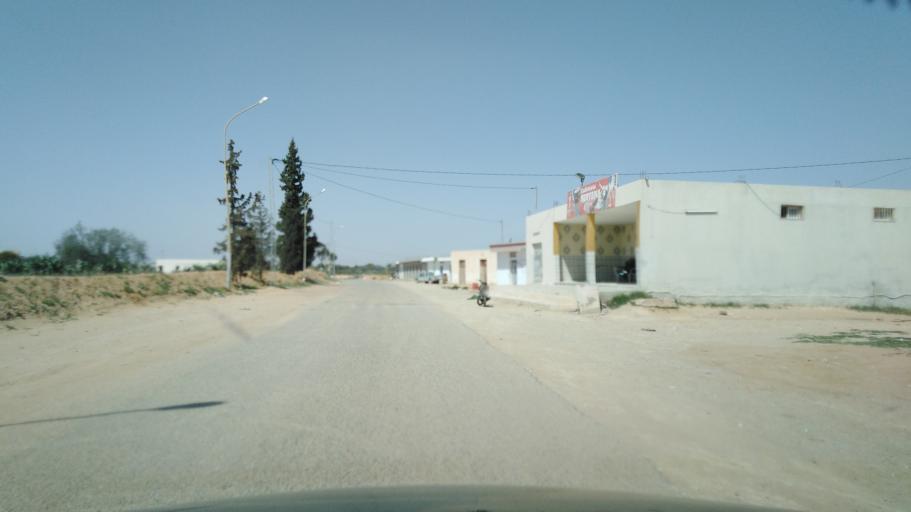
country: TN
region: Safaqis
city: Sfax
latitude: 34.6810
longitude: 10.4329
